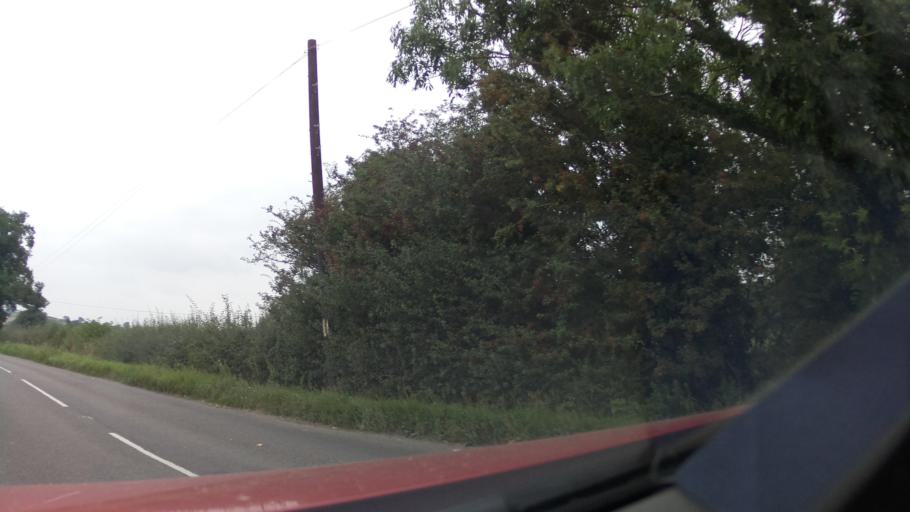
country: GB
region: England
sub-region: Derbyshire
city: Duffield
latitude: 52.9990
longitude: -1.5279
